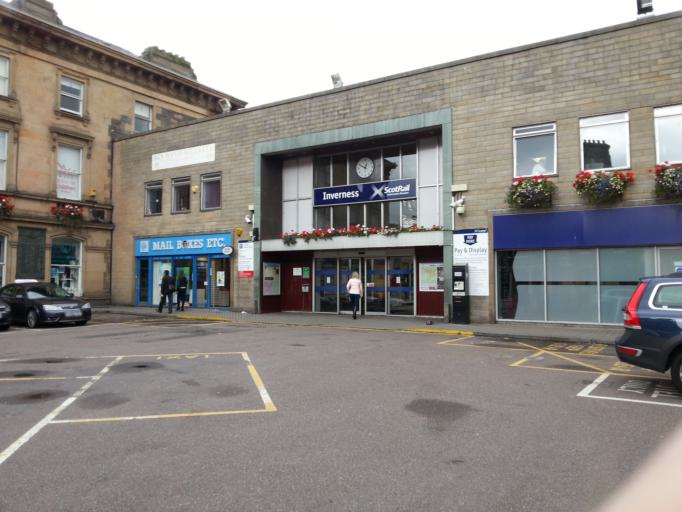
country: GB
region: Scotland
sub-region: Highland
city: Inverness
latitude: 57.4792
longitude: -4.2240
